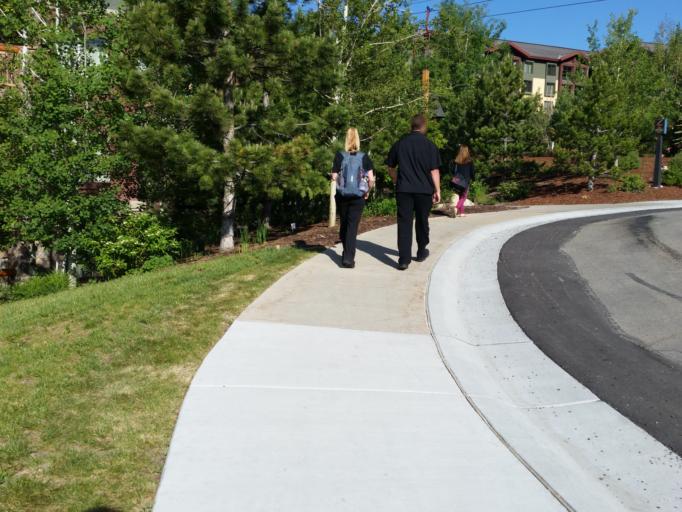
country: US
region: Utah
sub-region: Summit County
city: Snyderville
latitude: 40.6854
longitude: -111.5550
